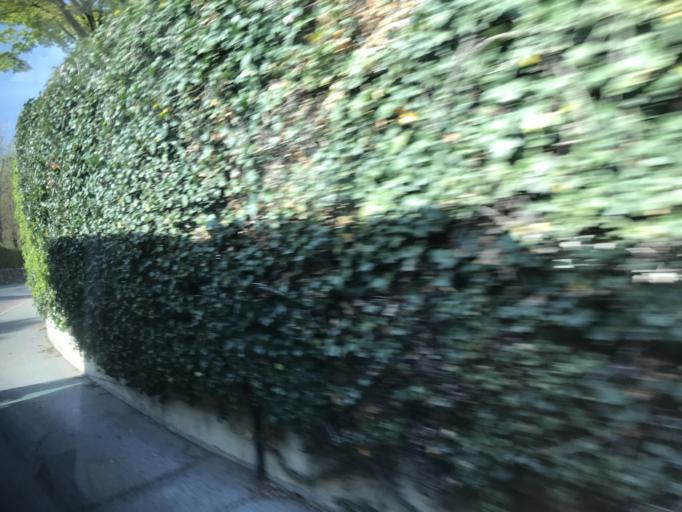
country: CH
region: Ticino
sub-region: Lugano District
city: Montagnola
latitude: 45.9865
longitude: 8.9204
